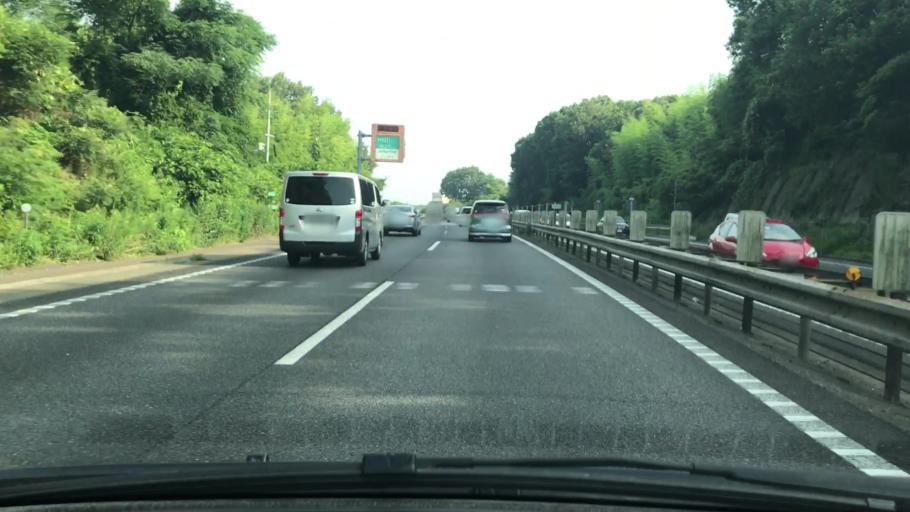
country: JP
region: Hyogo
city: Akashi
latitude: 34.6951
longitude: 134.9686
